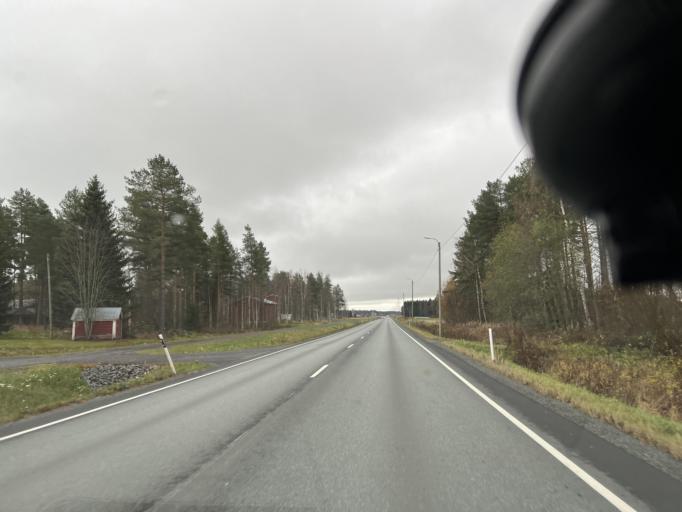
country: FI
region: Northern Ostrobothnia
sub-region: Ylivieska
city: Sievi
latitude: 63.9628
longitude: 24.5015
